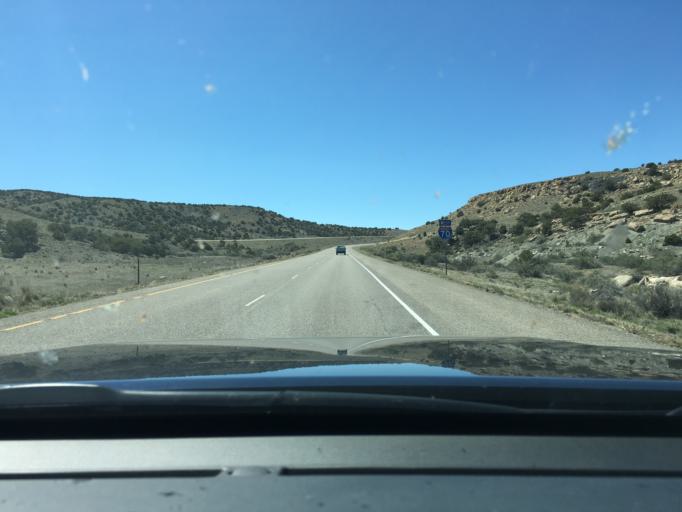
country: US
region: Colorado
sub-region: Mesa County
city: Loma
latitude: 39.1897
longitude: -109.0273
